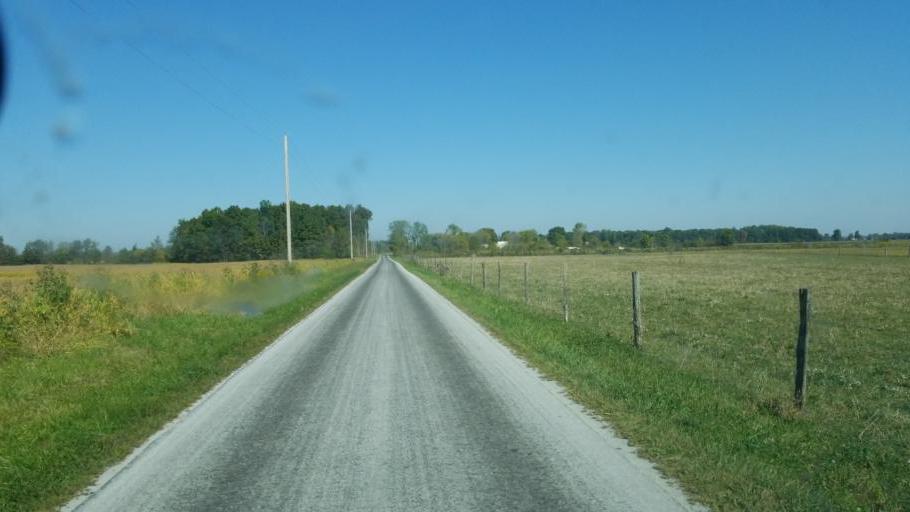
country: US
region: Ohio
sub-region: Hardin County
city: Kenton
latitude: 40.5707
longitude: -83.4880
